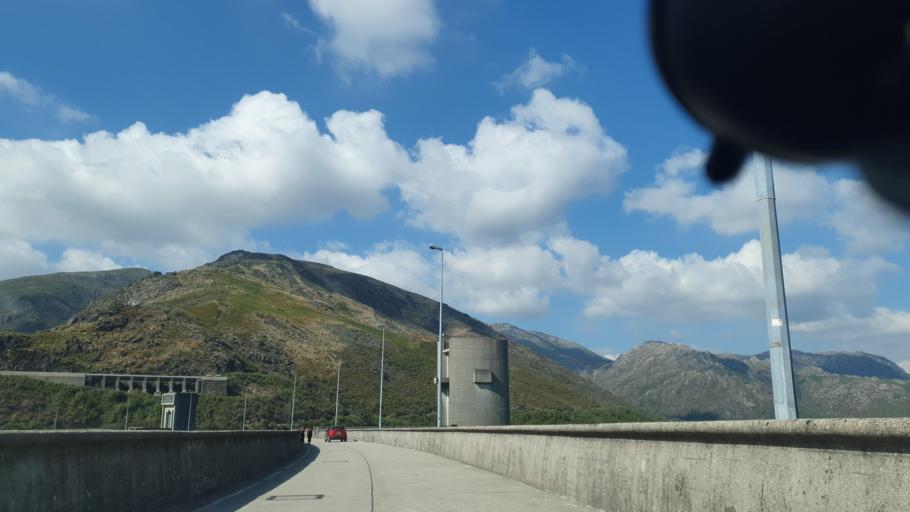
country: PT
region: Braga
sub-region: Terras de Bouro
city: Antas
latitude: 41.7622
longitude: -8.2086
